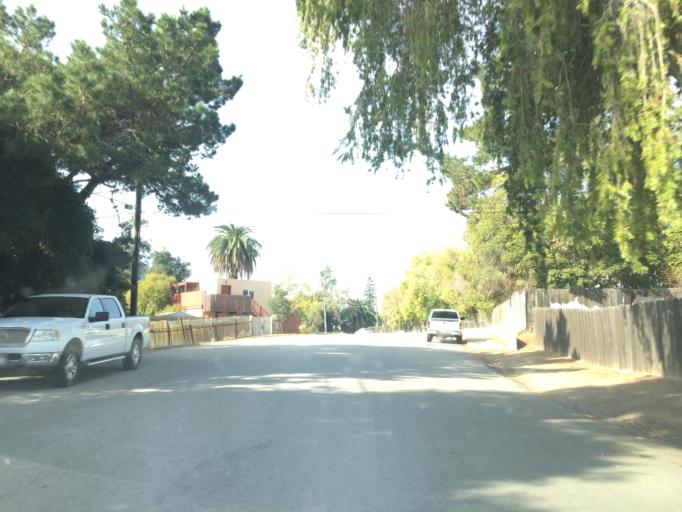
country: US
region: California
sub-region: San Luis Obispo County
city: San Luis Obispo
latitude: 35.2891
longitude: -120.6623
